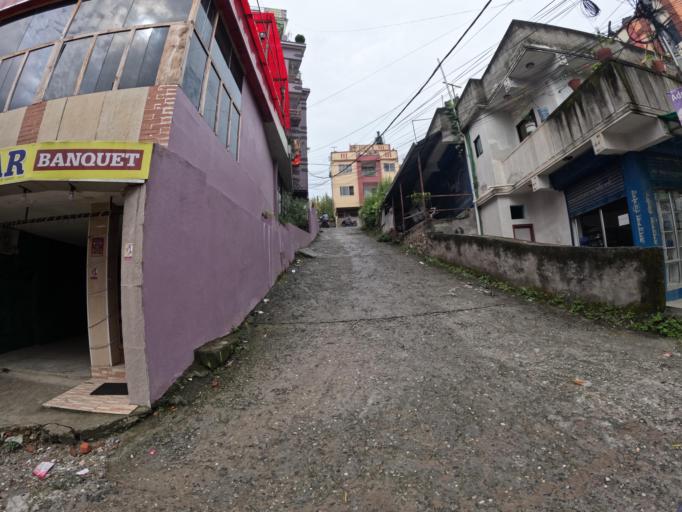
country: NP
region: Central Region
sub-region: Bagmati Zone
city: Kathmandu
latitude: 27.7562
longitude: 85.3227
